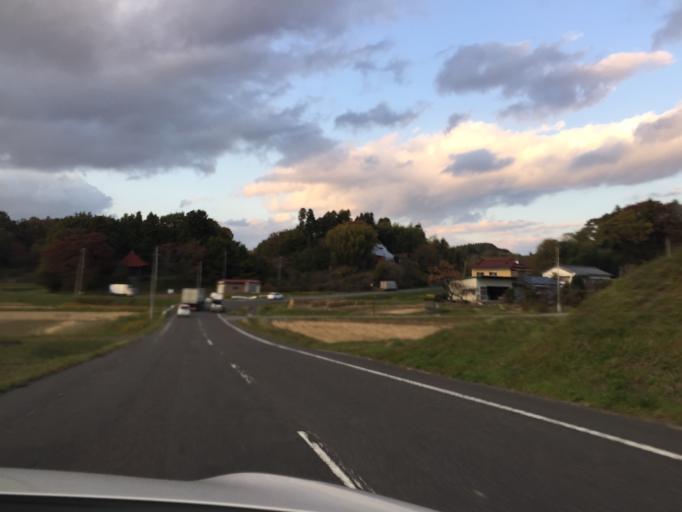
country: JP
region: Fukushima
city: Miharu
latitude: 37.4696
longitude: 140.4408
